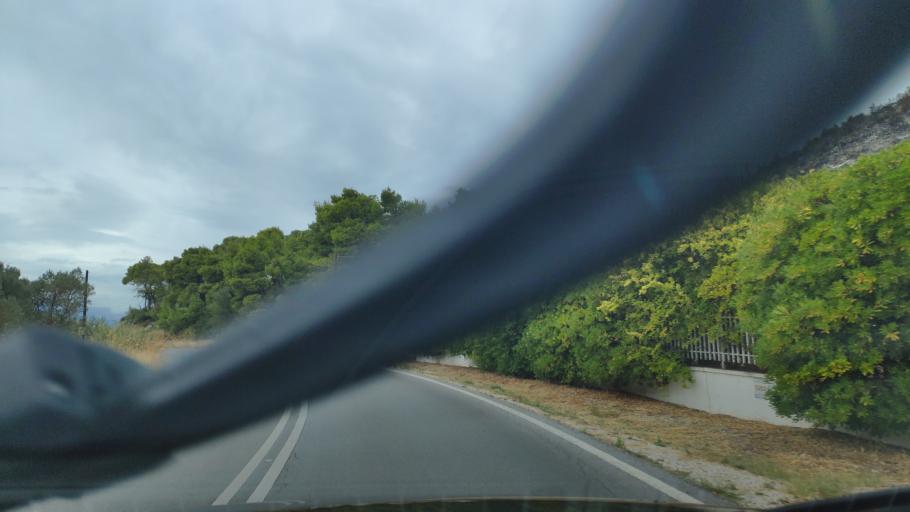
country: GR
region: Peloponnese
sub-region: Nomos Korinthias
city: Perachora
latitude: 38.0292
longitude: 22.9329
